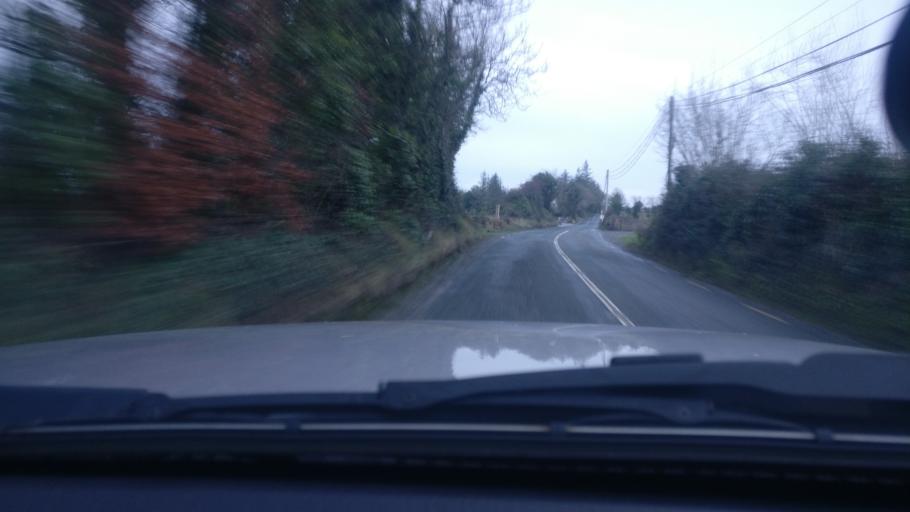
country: IE
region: Connaught
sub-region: County Galway
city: Loughrea
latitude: 53.1692
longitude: -8.5228
